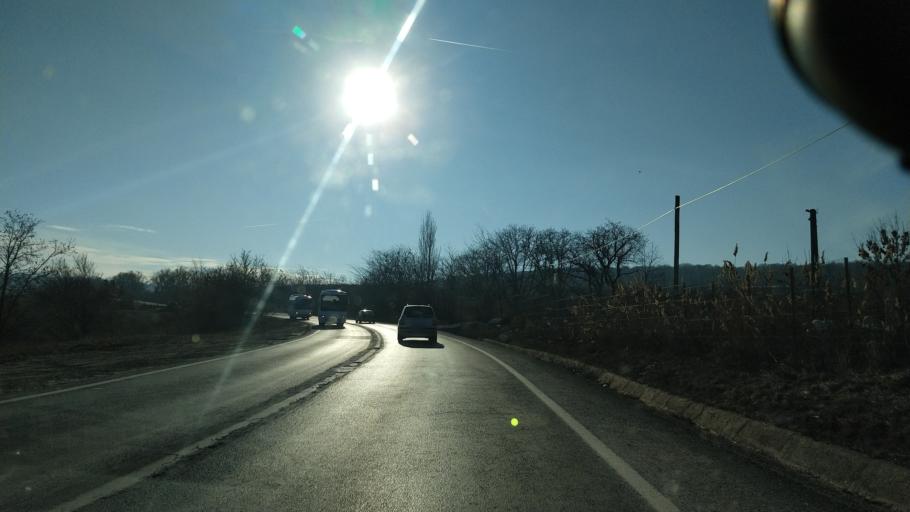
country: RO
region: Iasi
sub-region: Comuna Strunga
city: Strunga
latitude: 47.1772
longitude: 26.9538
